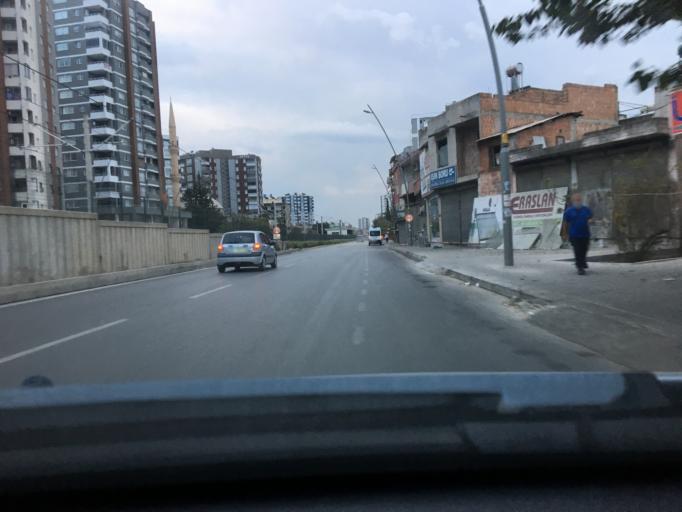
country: TR
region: Adana
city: Seyhan
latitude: 37.0287
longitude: 35.2940
